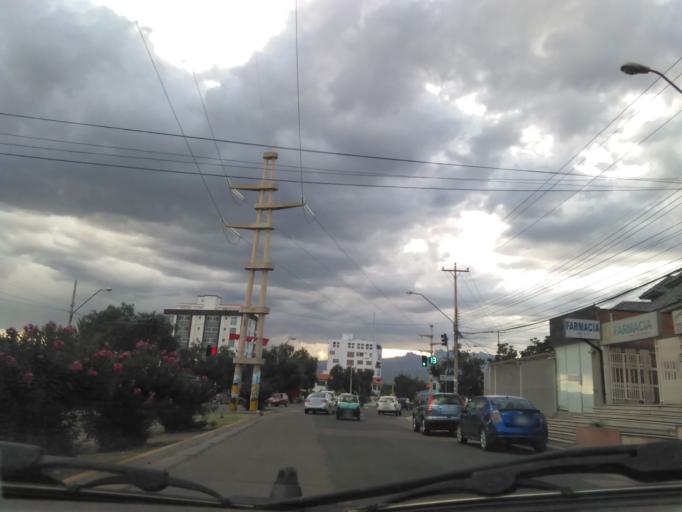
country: BO
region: Cochabamba
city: Cochabamba
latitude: -17.3664
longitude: -66.1564
